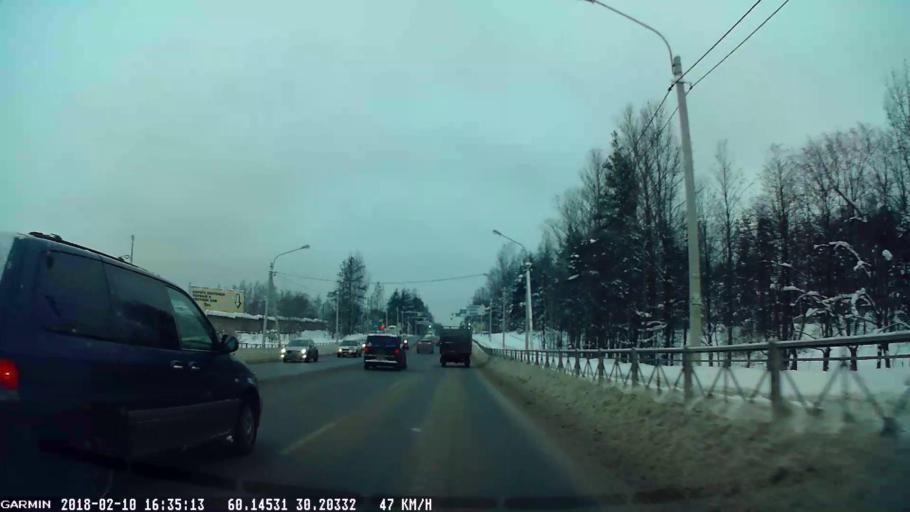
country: RU
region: Leningrad
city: Sertolovo
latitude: 60.1460
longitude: 30.2024
